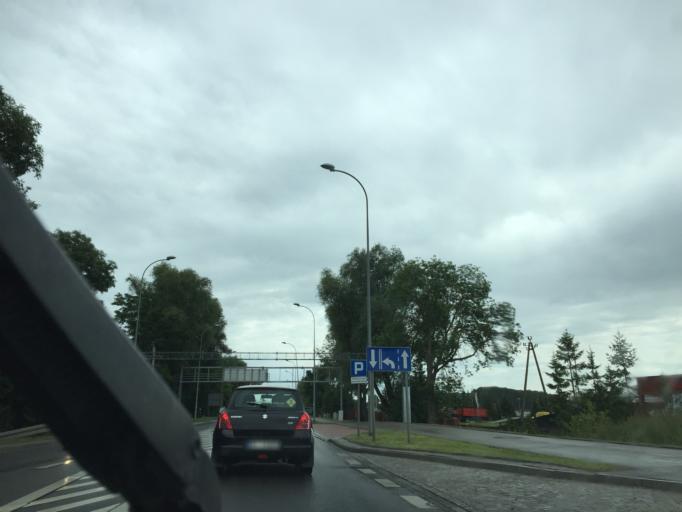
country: PL
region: Podlasie
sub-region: Bialystok
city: Bialystok
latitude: 53.0965
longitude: 23.2335
